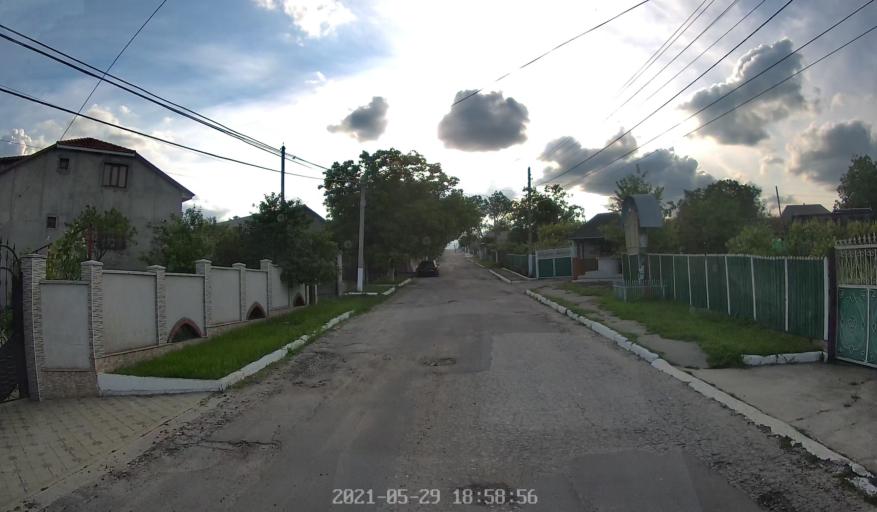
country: MD
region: Chisinau
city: Singera
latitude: 46.8258
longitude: 28.9686
